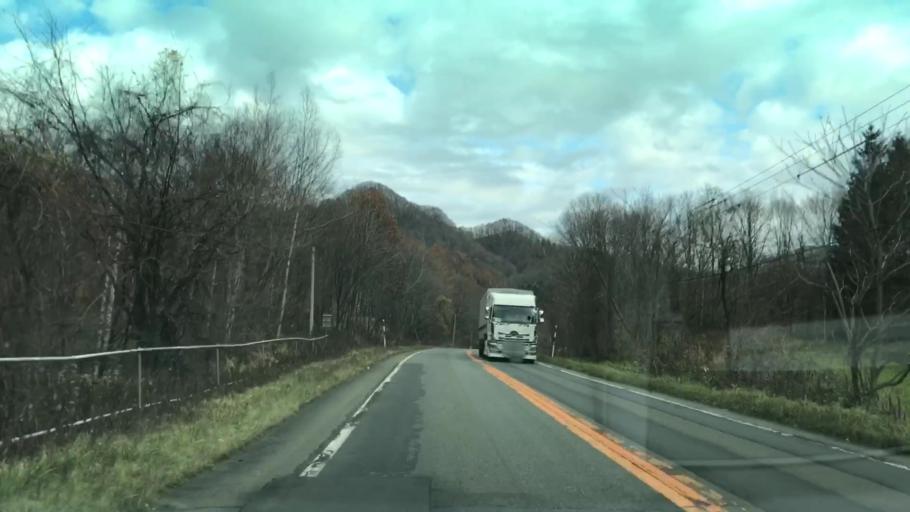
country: JP
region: Hokkaido
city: Shizunai-furukawacho
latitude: 42.8103
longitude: 142.4042
